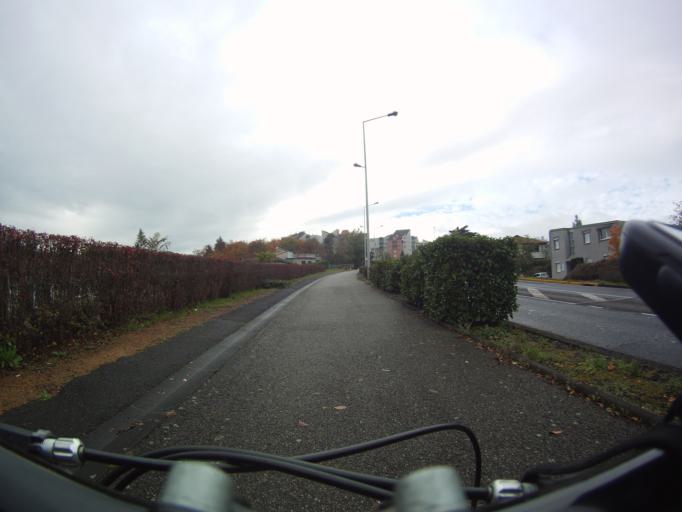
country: FR
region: Auvergne
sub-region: Departement du Puy-de-Dome
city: Aubiere
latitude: 45.7555
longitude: 3.0981
